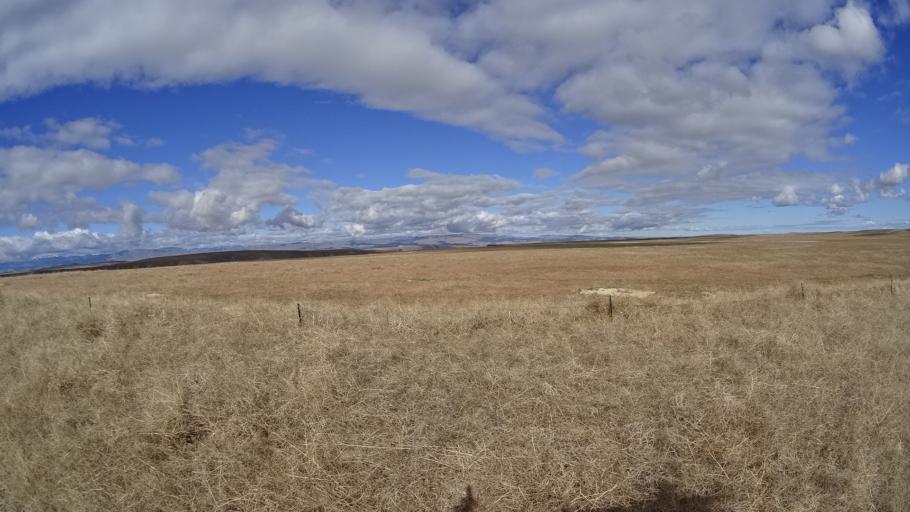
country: US
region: Idaho
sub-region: Owyhee County
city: Murphy
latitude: 43.2927
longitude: -116.3942
